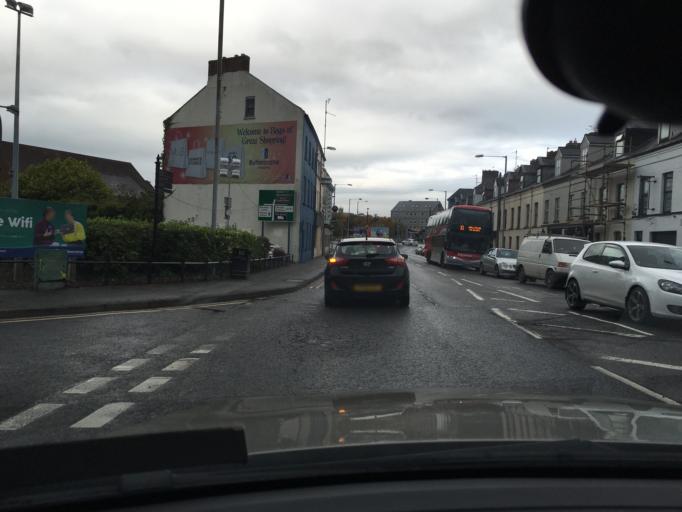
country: GB
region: Northern Ireland
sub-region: Newry and Mourne District
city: Newry
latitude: 54.1702
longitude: -6.3413
